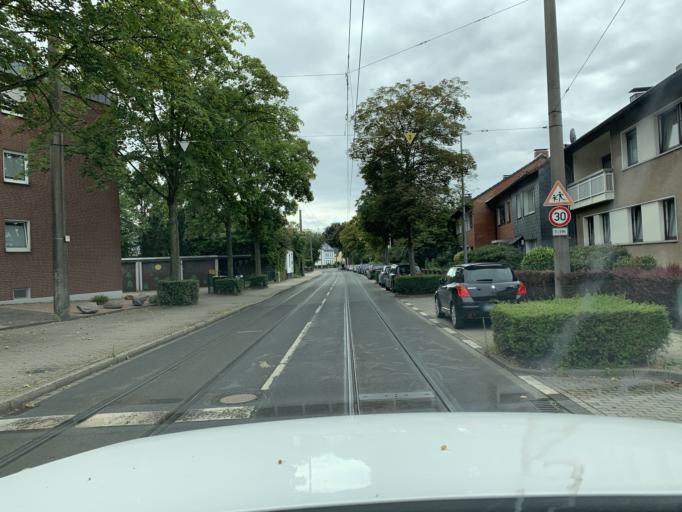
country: DE
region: North Rhine-Westphalia
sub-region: Regierungsbezirk Dusseldorf
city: Oberhausen
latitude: 51.4618
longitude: 6.9057
